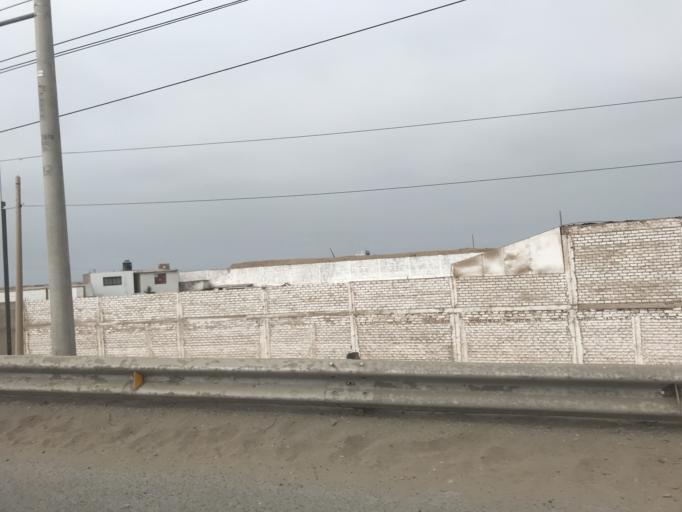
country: PE
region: Lima
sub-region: Lima
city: Punta Hermosa
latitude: -12.2565
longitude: -76.9236
